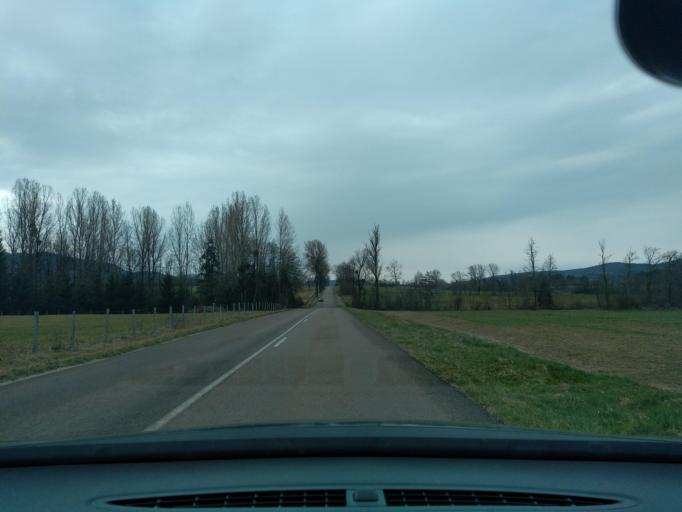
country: FR
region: Franche-Comte
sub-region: Departement du Jura
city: Arinthod
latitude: 46.3733
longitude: 5.5620
